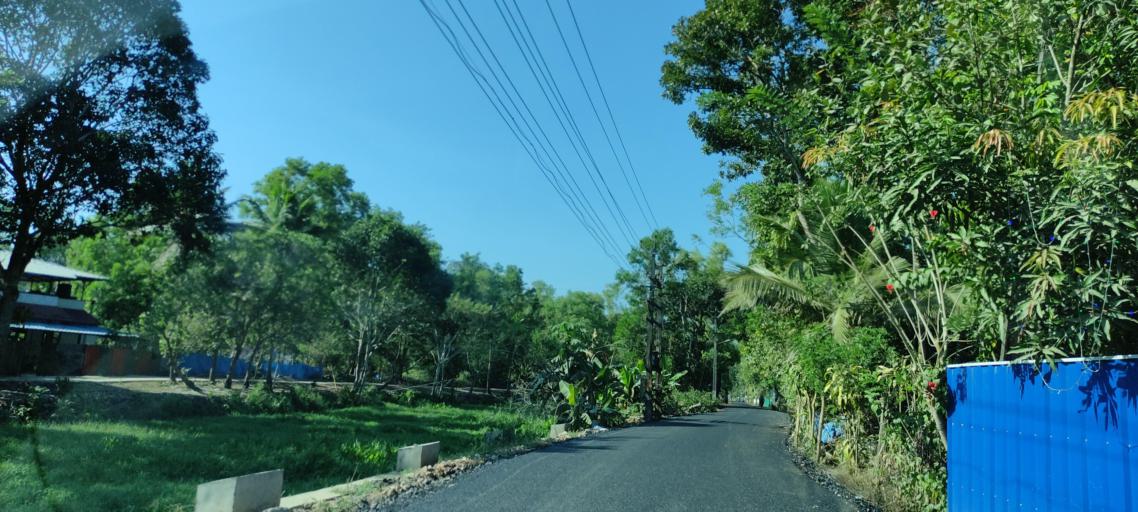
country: IN
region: Kerala
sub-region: Alappuzha
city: Shertallai
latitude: 9.6119
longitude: 76.3327
